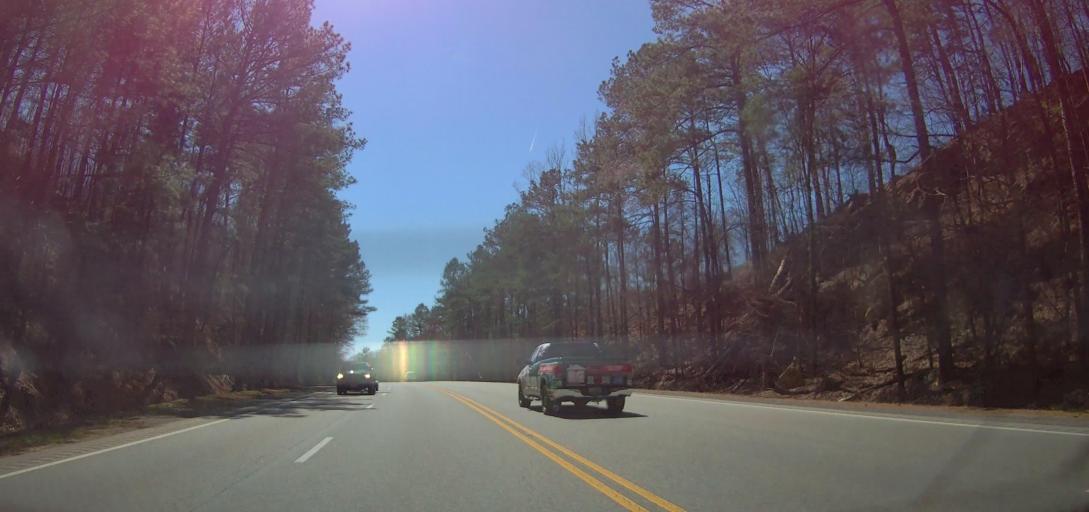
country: US
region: Alabama
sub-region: Calhoun County
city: Ohatchee
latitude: 33.8438
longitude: -86.0507
